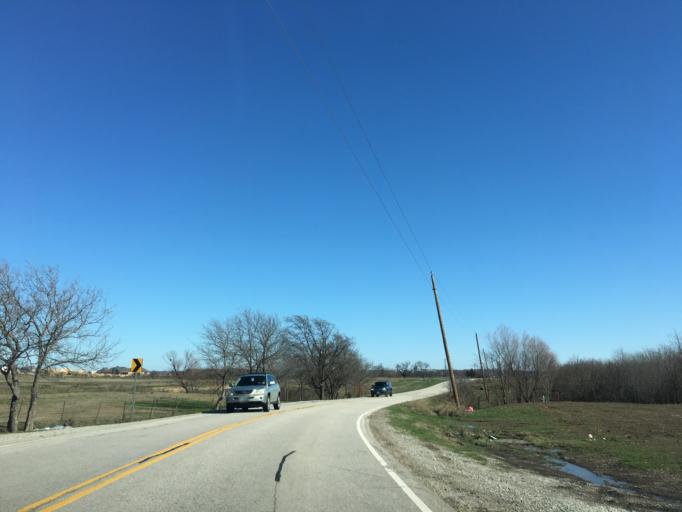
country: US
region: Texas
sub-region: Collin County
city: Prosper
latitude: 33.2333
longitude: -96.8335
